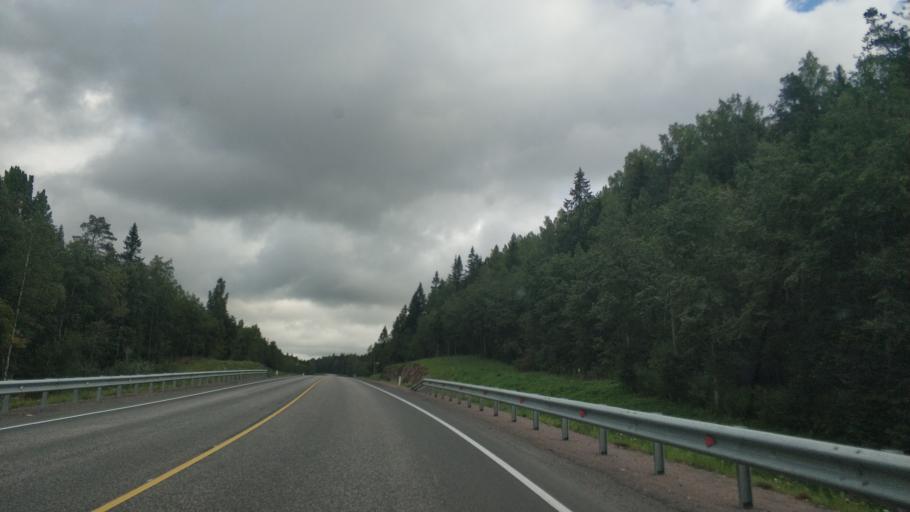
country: RU
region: Republic of Karelia
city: Khelyulya
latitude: 61.8327
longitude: 30.6391
